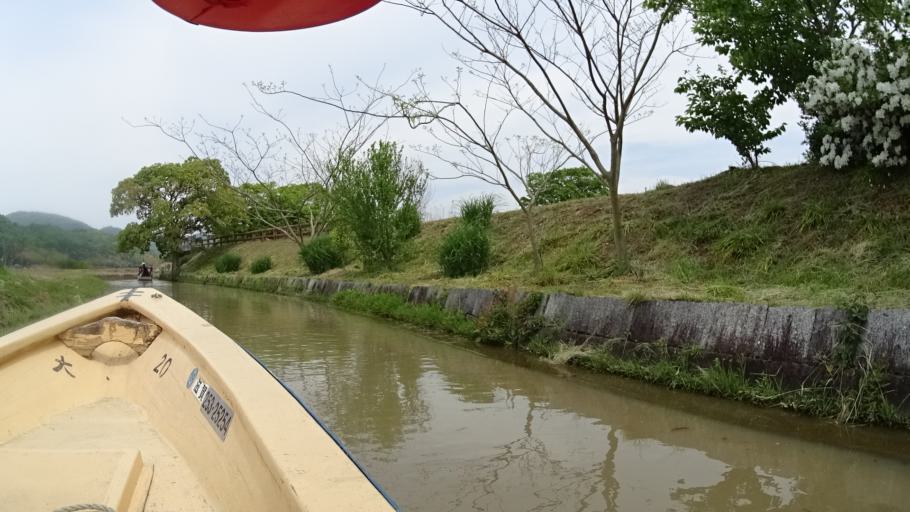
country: JP
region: Shiga Prefecture
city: Omihachiman
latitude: 35.1539
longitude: 136.0998
